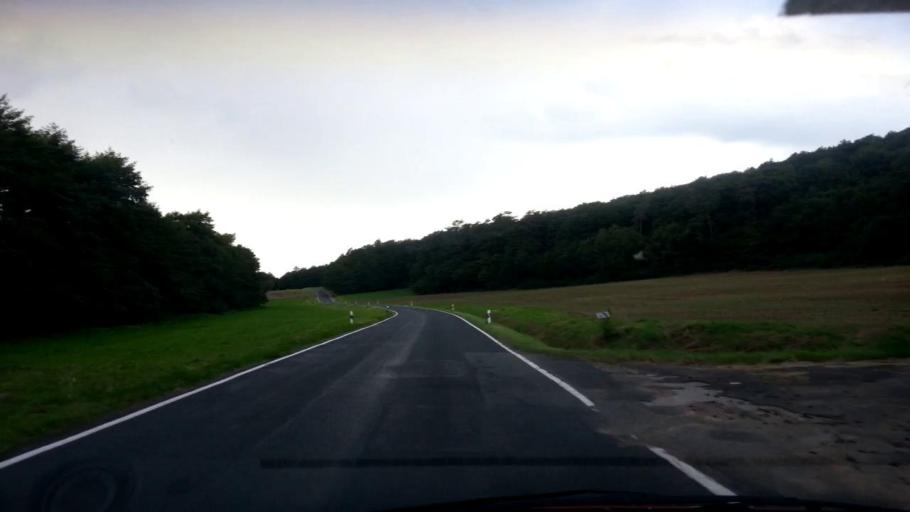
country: DE
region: Bavaria
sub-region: Regierungsbezirk Unterfranken
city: Geiselwind
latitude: 49.7491
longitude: 10.5050
